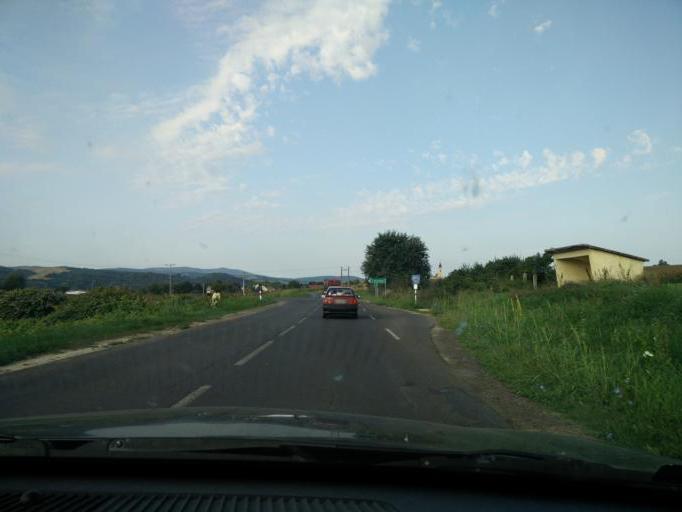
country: HU
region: Tolna
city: Nagymanyok
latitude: 46.2863
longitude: 18.4714
